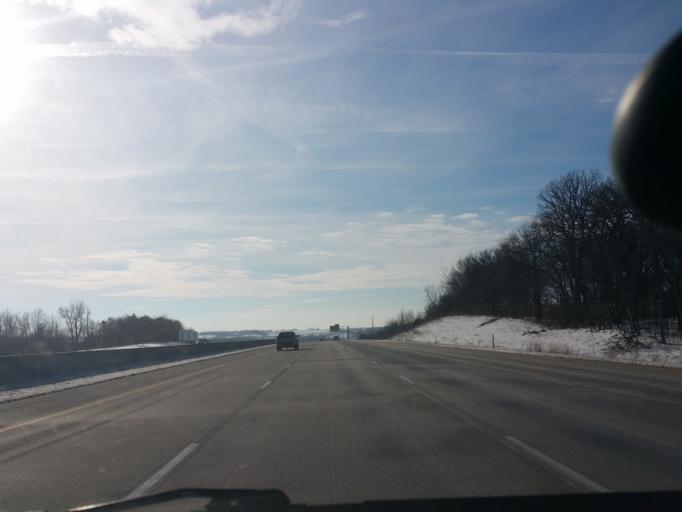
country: US
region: Iowa
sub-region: Polk County
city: West Des Moines
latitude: 41.5501
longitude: -93.7764
